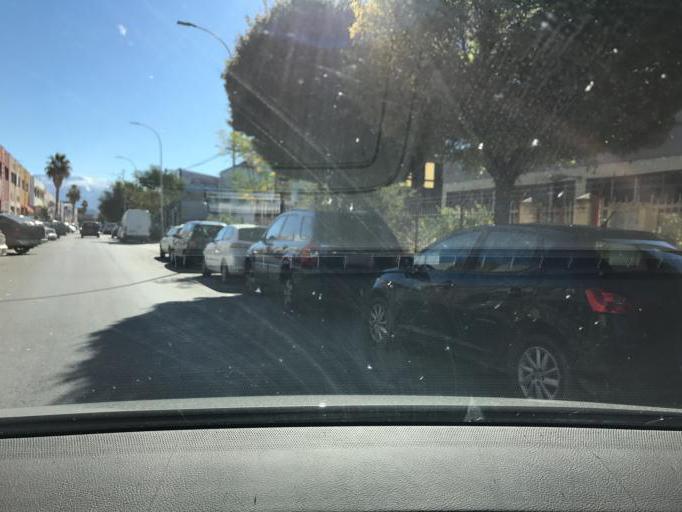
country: ES
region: Andalusia
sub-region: Provincia de Granada
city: Albolote
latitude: 37.2285
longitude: -3.6441
